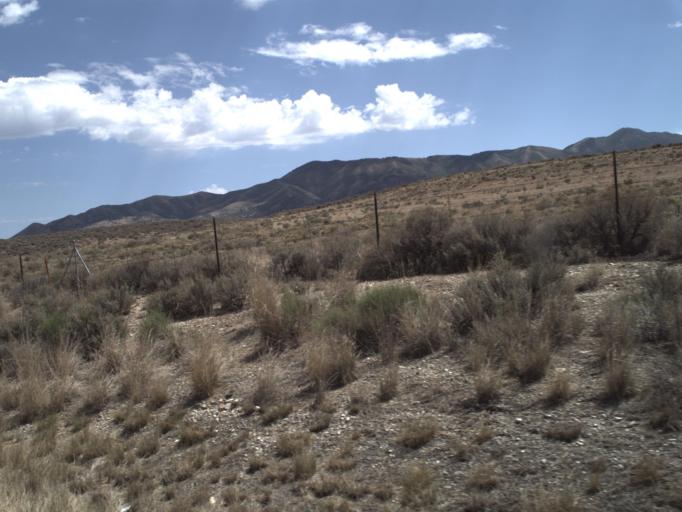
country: US
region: Utah
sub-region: Tooele County
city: Tooele
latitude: 40.4131
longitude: -112.3837
